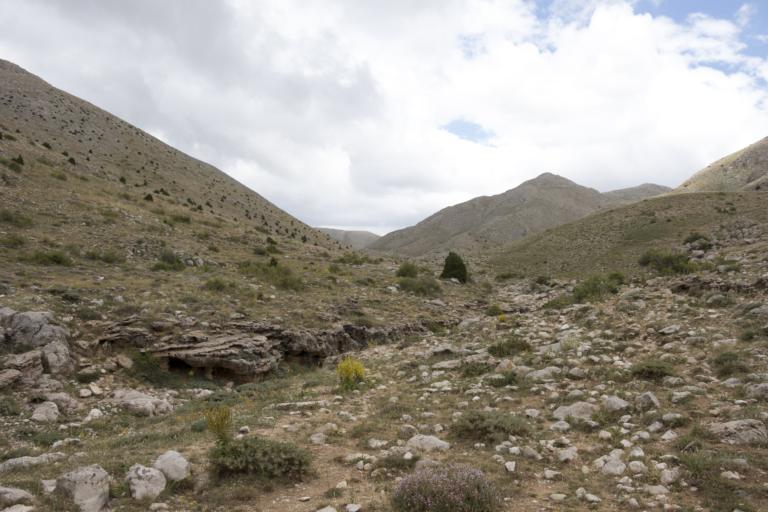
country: TR
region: Kayseri
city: Toklar
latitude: 38.4328
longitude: 36.1740
